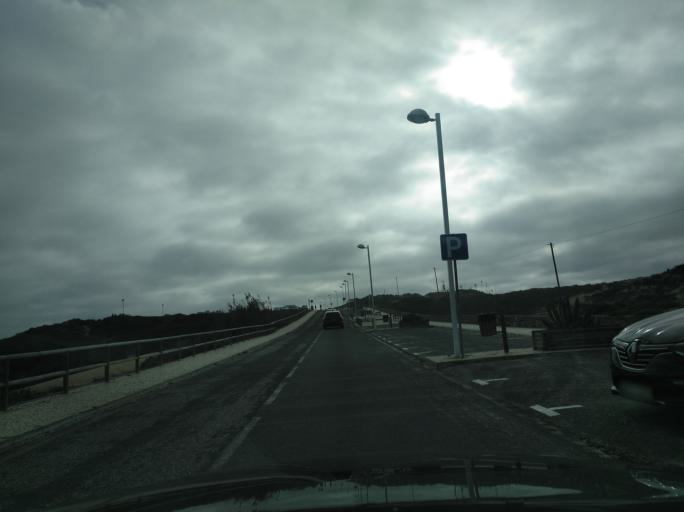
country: PT
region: Beja
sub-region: Odemira
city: Vila Nova de Milfontes
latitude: 37.7217
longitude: -8.7886
